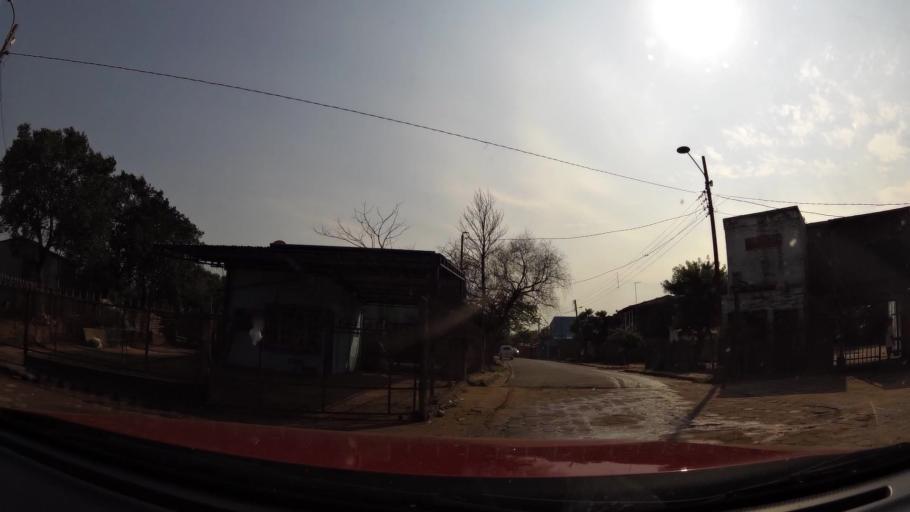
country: PY
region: Asuncion
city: Asuncion
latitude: -25.3155
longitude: -57.6701
